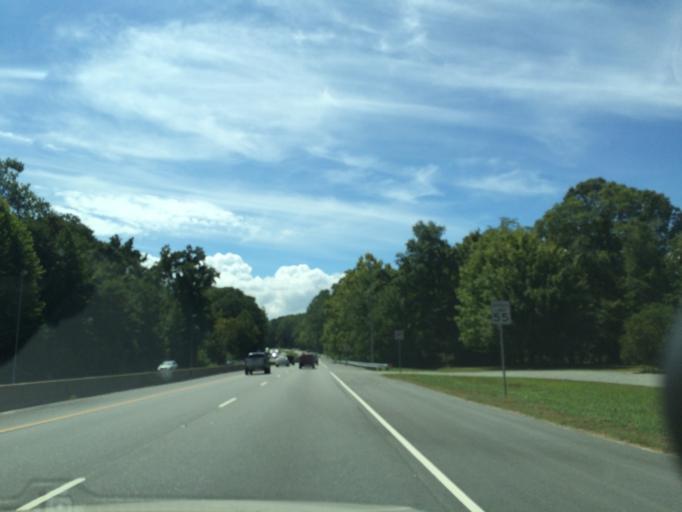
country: US
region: Virginia
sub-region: York County
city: Yorktown
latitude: 37.2340
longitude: -76.5131
